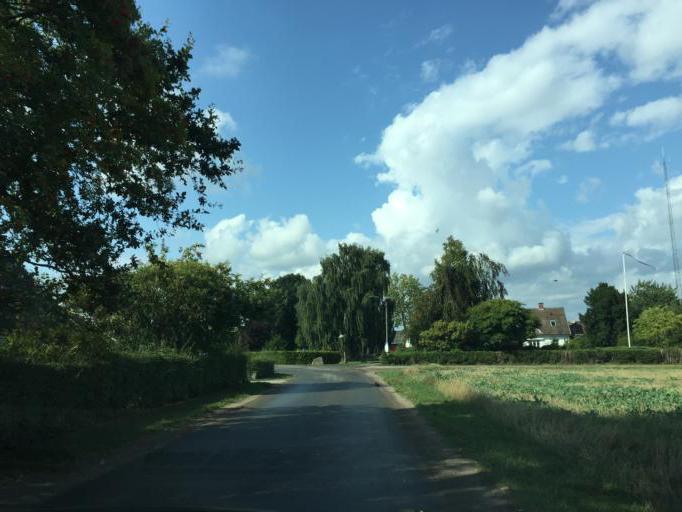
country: DK
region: South Denmark
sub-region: Odense Kommune
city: Bellinge
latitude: 55.3338
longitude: 10.3764
